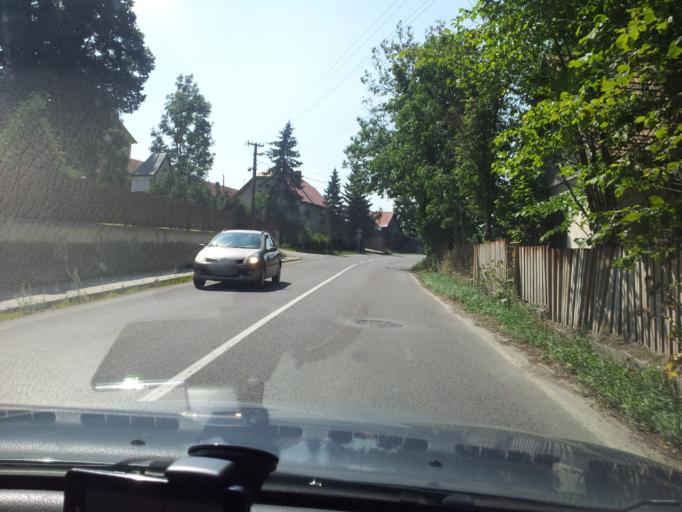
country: SK
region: Zilinsky
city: Namestovo
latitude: 49.3640
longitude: 19.4075
